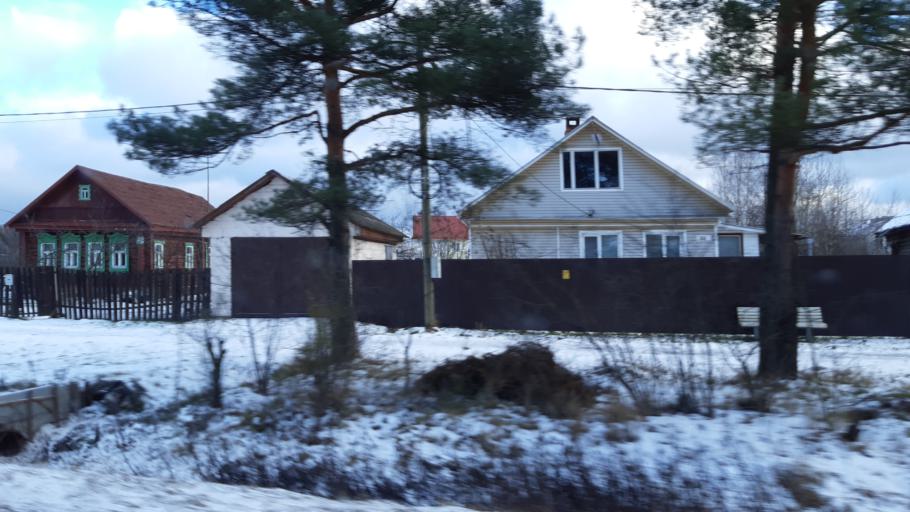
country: RU
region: Moskovskaya
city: Noginsk-9
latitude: 55.9940
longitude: 38.5430
